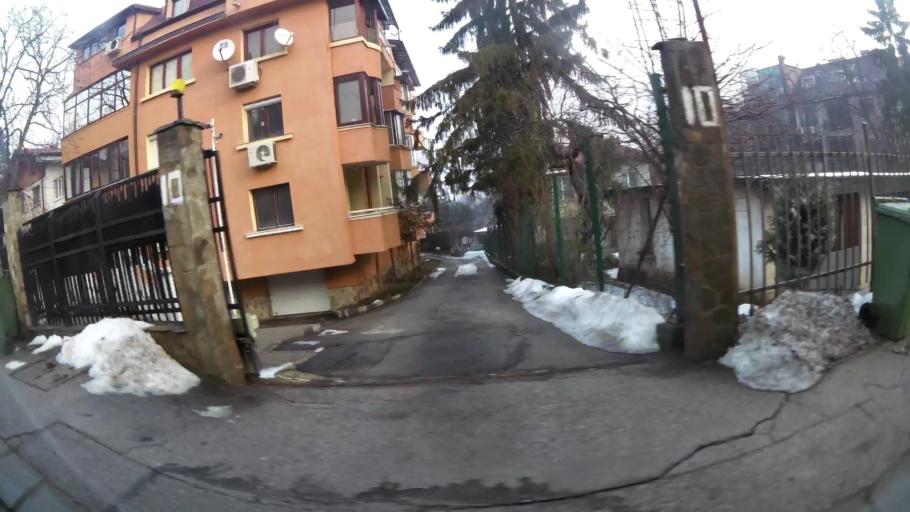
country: BG
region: Sofia-Capital
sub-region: Stolichna Obshtina
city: Sofia
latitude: 42.6515
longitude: 23.2579
